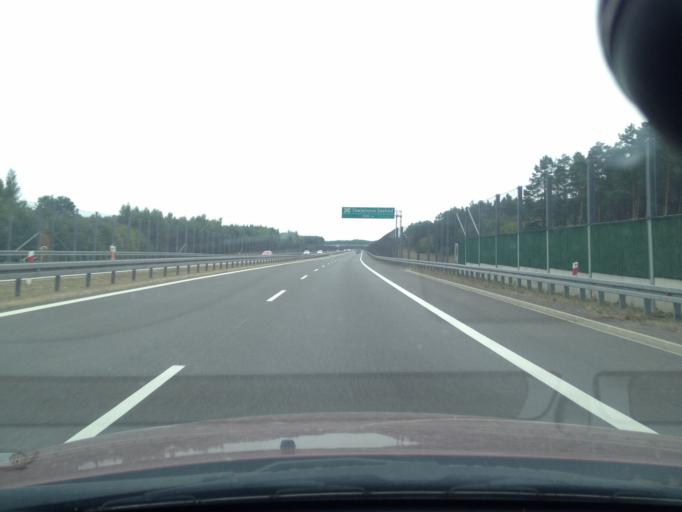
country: PL
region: Lubusz
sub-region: Powiat miedzyrzecki
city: Skwierzyna
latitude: 52.5619
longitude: 15.4746
